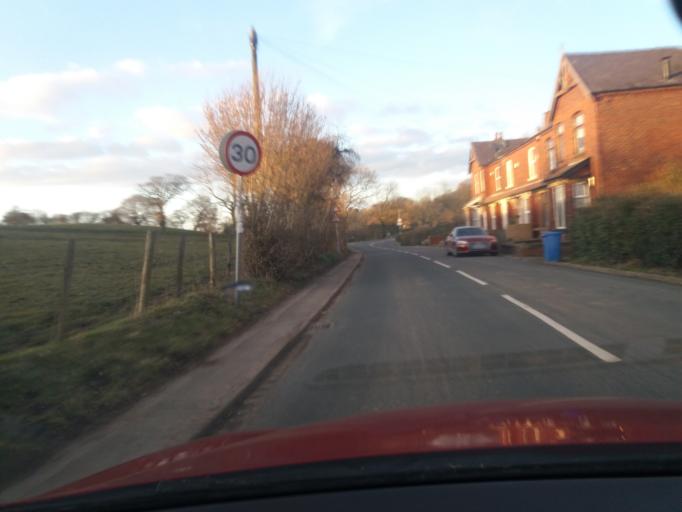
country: GB
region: England
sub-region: Lancashire
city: Chorley
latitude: 53.6778
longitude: -2.6213
